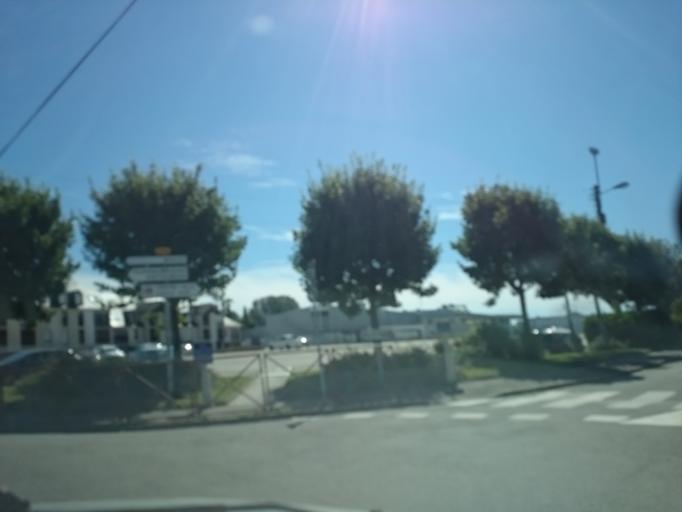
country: FR
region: Brittany
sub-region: Departement du Finistere
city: Saint-Renan
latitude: 48.4347
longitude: -4.6217
